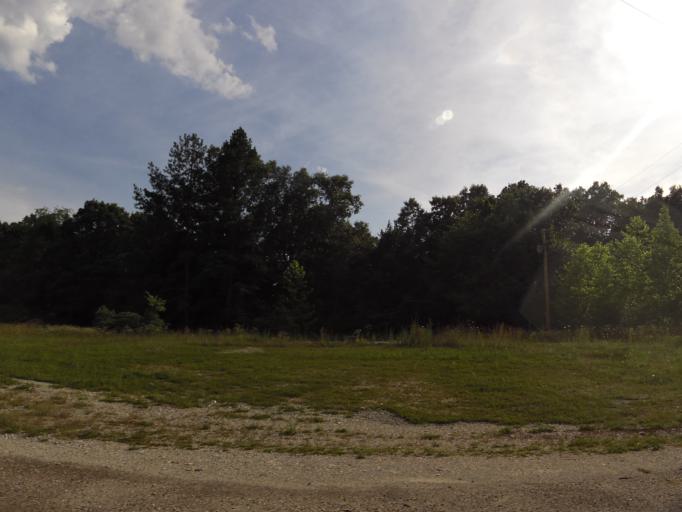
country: US
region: Tennessee
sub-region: Benton County
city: Camden
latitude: 36.0229
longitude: -88.0640
